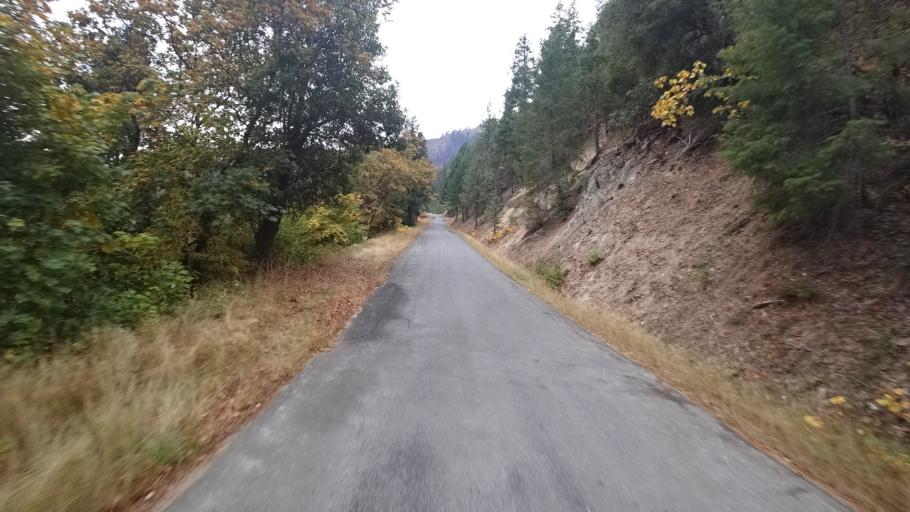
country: US
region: California
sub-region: Siskiyou County
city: Happy Camp
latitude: 41.8321
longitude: -123.1966
